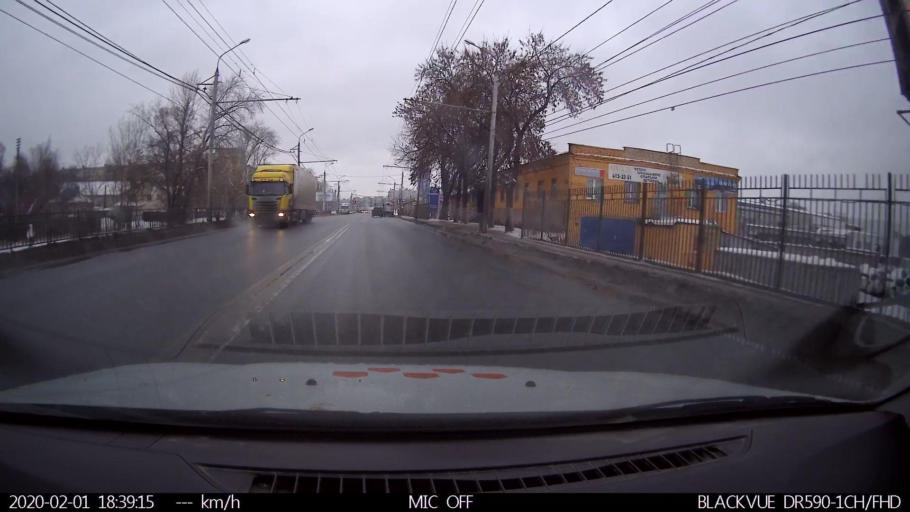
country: RU
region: Nizjnij Novgorod
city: Nizhniy Novgorod
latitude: 56.3325
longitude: 43.9226
